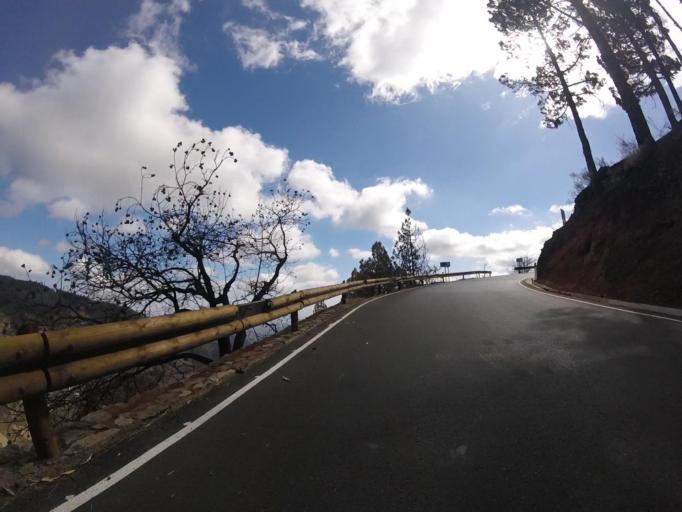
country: ES
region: Canary Islands
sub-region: Provincia de Las Palmas
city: Tejeda
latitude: 28.0027
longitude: -15.5943
